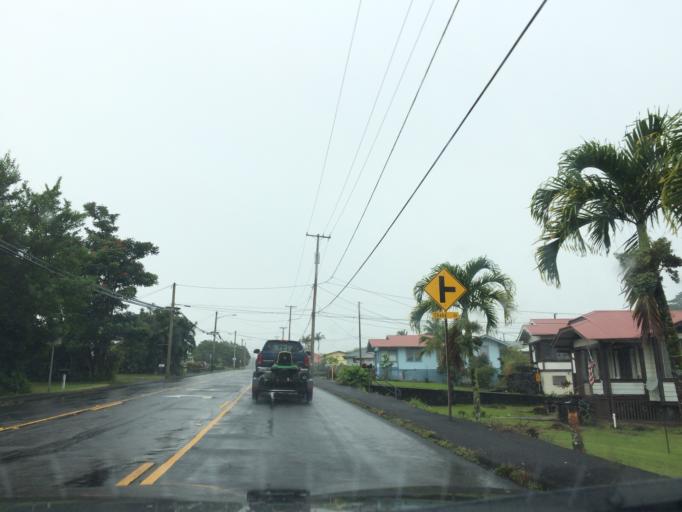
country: US
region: Hawaii
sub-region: Hawaii County
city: Hilo
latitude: 19.7130
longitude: -155.1069
